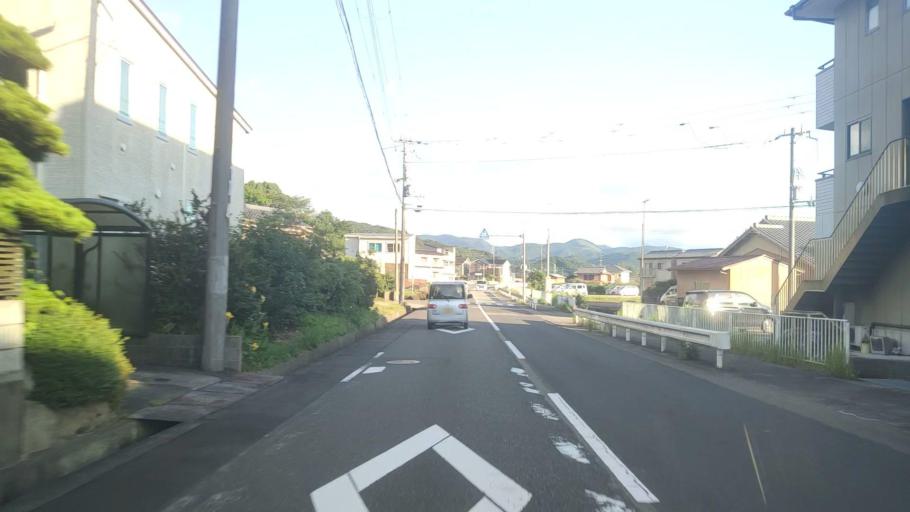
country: JP
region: Wakayama
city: Tanabe
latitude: 33.7226
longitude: 135.4452
